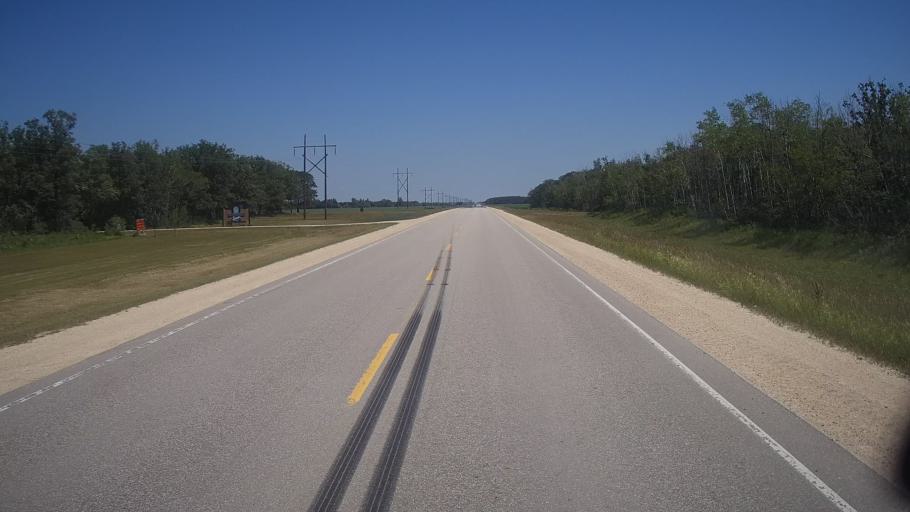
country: CA
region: Manitoba
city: Stonewall
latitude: 50.1228
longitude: -97.4770
